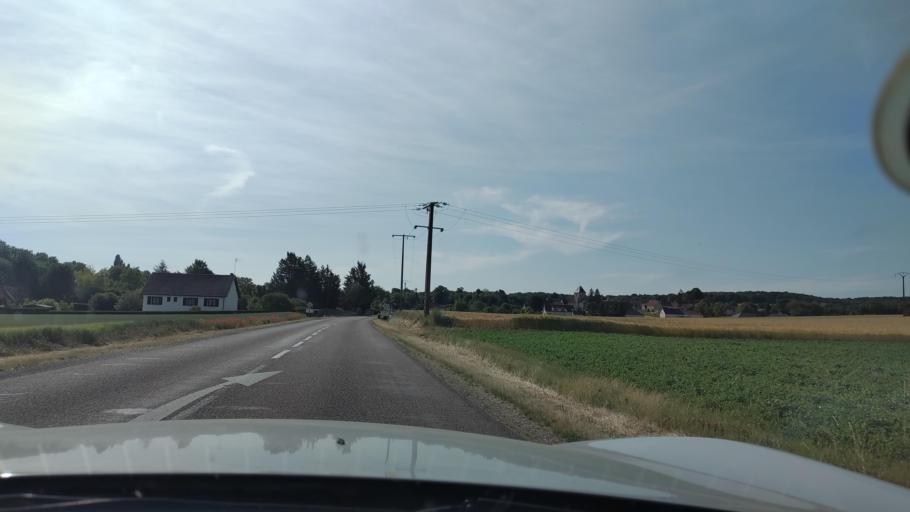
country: FR
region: Champagne-Ardenne
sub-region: Departement de l'Aube
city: Nogent-sur-Seine
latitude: 48.4544
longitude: 3.6059
